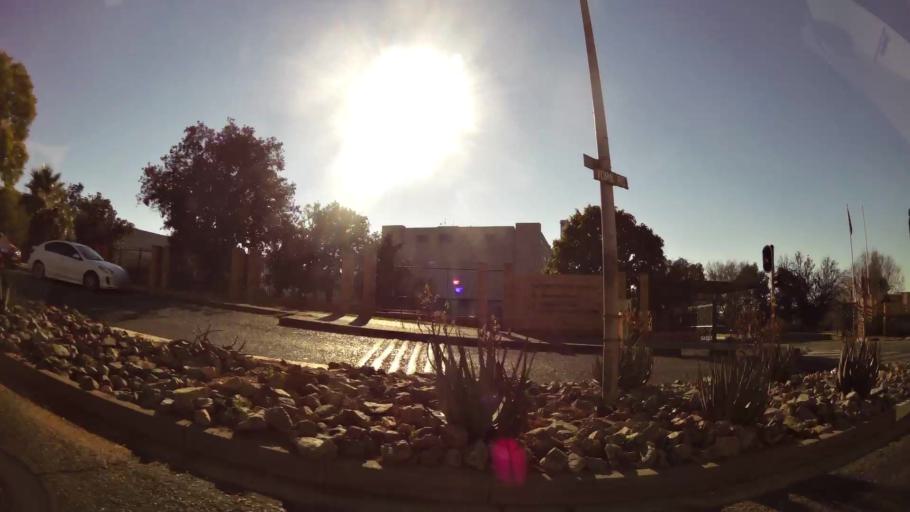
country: ZA
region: Gauteng
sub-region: City of Johannesburg Metropolitan Municipality
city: Johannesburg
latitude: -26.1770
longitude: 28.0449
